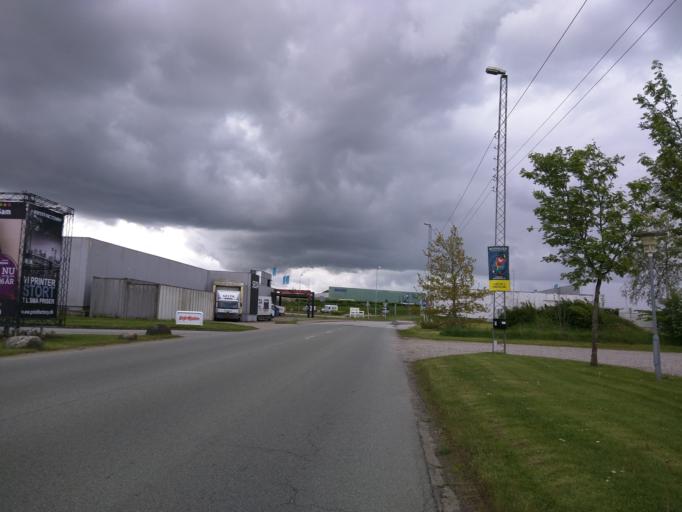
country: DK
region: Central Jutland
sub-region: Viborg Kommune
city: Viborg
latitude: 56.4499
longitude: 9.3683
